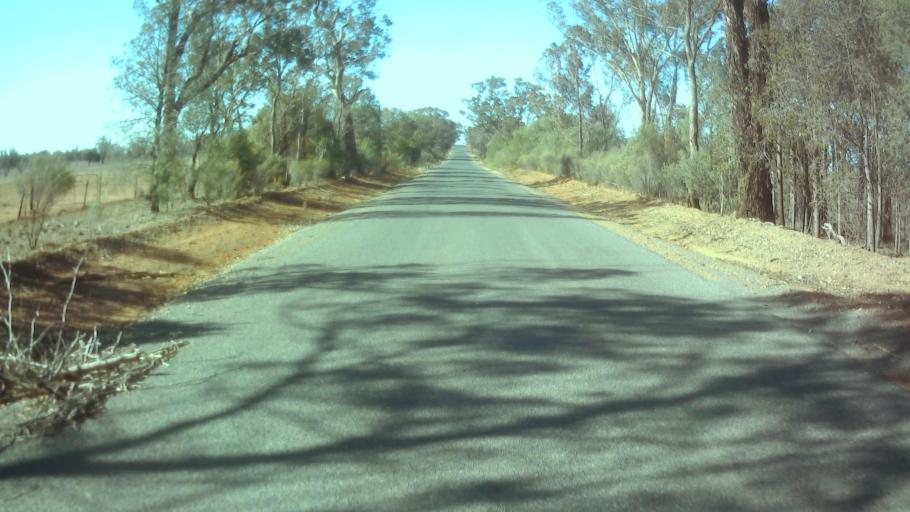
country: AU
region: New South Wales
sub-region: Forbes
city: Forbes
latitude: -33.7102
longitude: 147.8048
